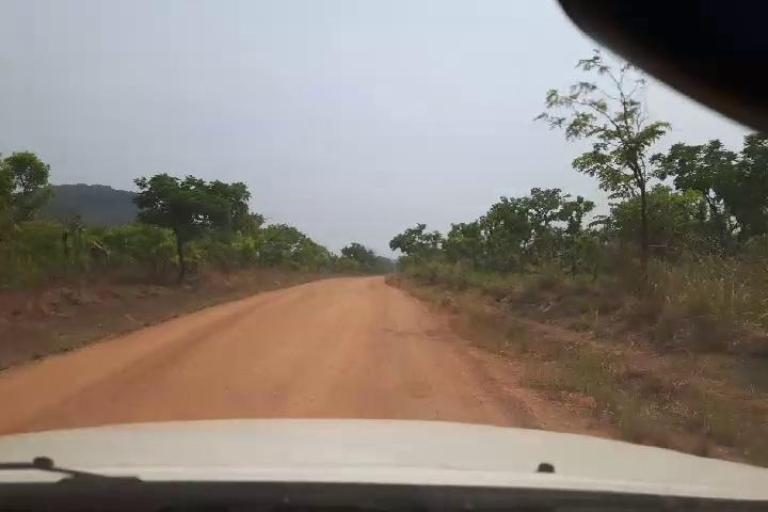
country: SL
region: Northern Province
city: Masingbi
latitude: 8.8893
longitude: -11.8184
